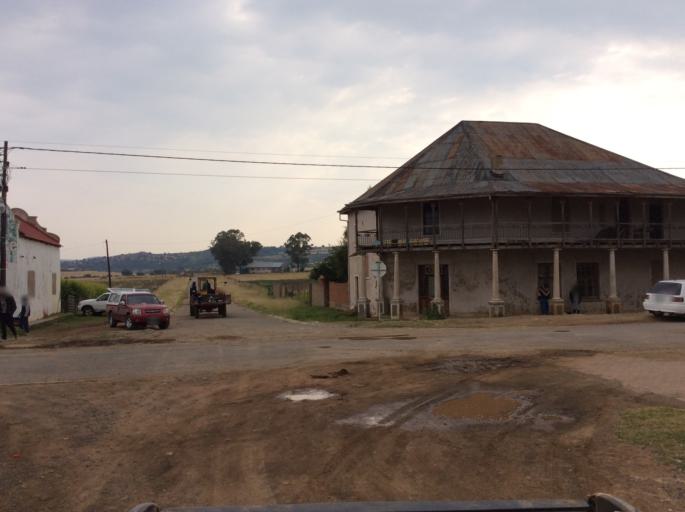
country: LS
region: Mafeteng
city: Mafeteng
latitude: -29.9878
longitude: 27.0144
